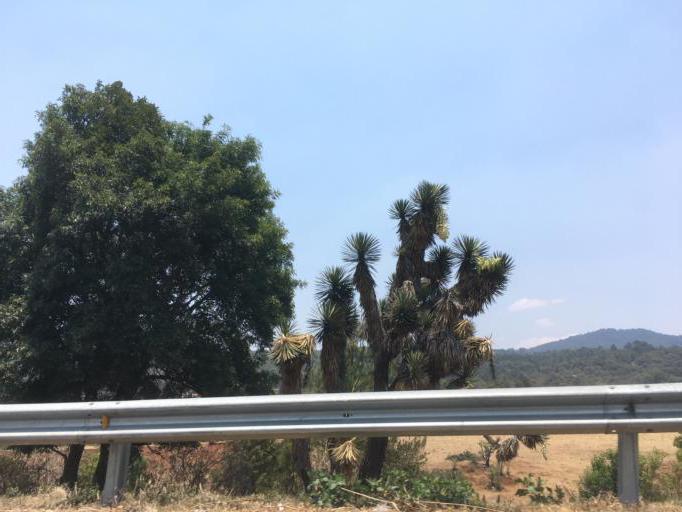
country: MX
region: Michoacan
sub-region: Morelia
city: Iratzio
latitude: 19.6346
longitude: -101.4699
